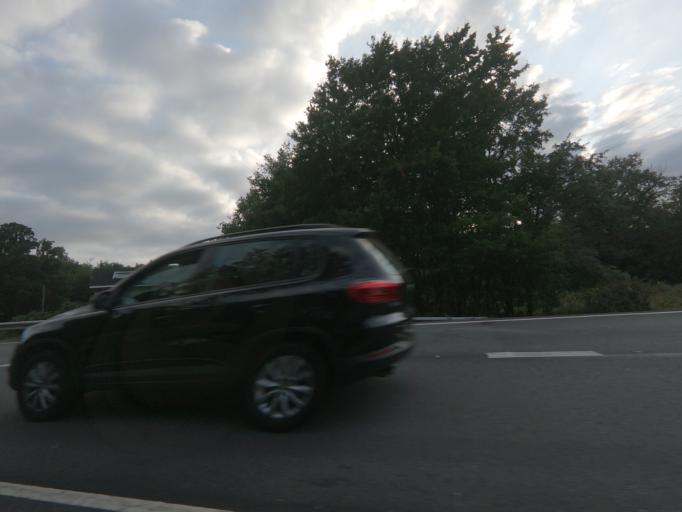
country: ES
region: Galicia
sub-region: Provincia de Ourense
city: Taboadela
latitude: 42.2452
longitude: -7.8425
